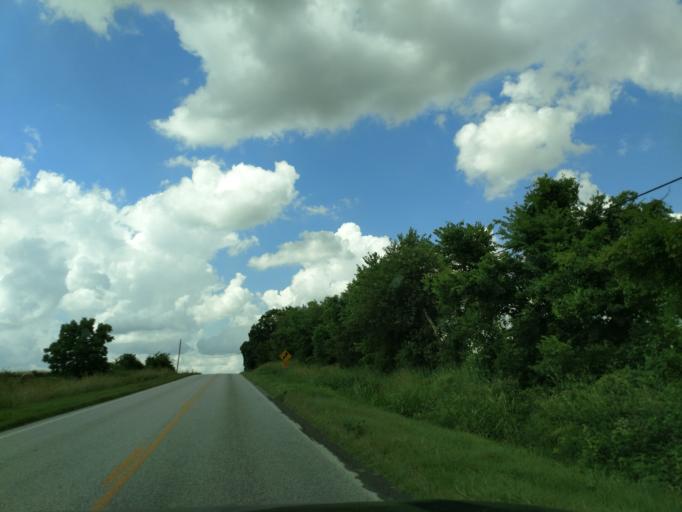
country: US
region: Arkansas
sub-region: Carroll County
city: Berryville
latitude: 36.4116
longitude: -93.5613
